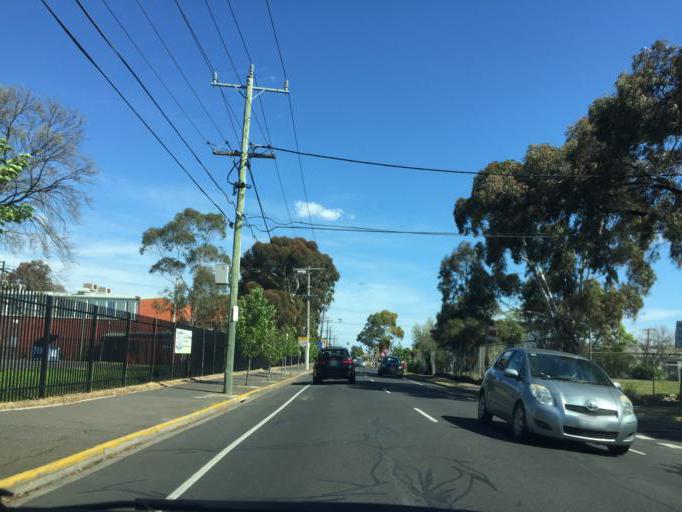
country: AU
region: Victoria
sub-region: Maribyrnong
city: Maribyrnong
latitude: -37.7865
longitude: 144.8835
